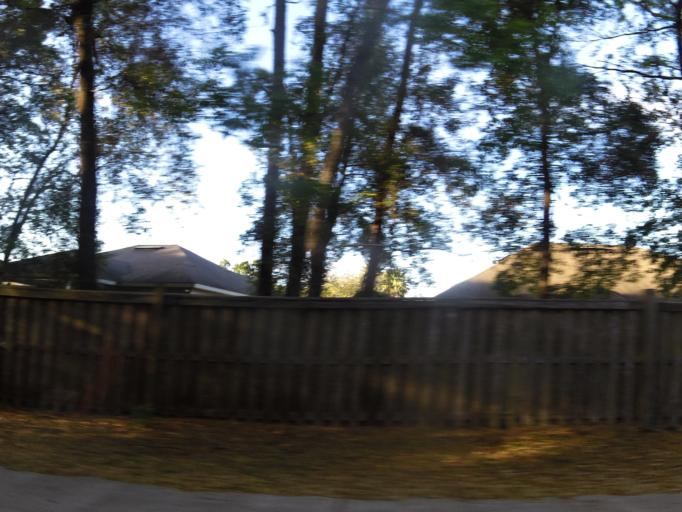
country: US
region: Florida
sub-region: Duval County
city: Jacksonville
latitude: 30.4398
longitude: -81.6228
